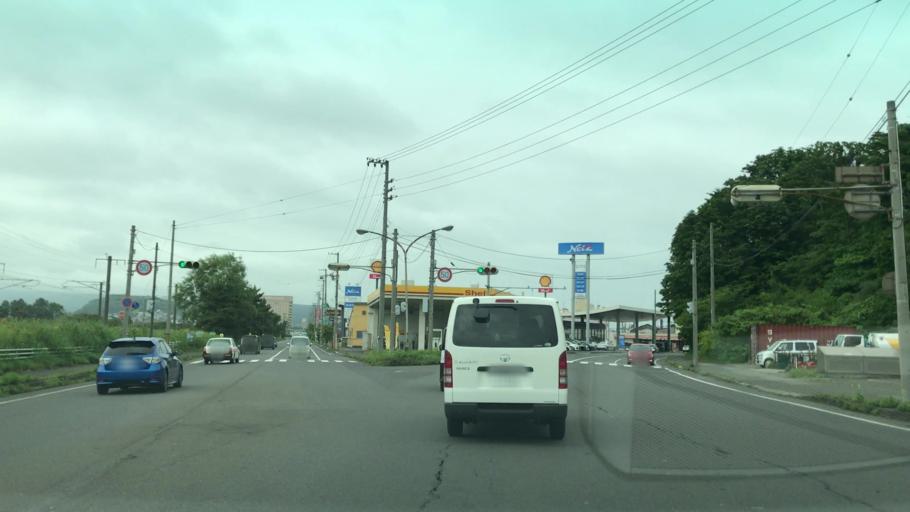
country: JP
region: Hokkaido
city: Muroran
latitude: 42.3407
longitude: 141.0169
